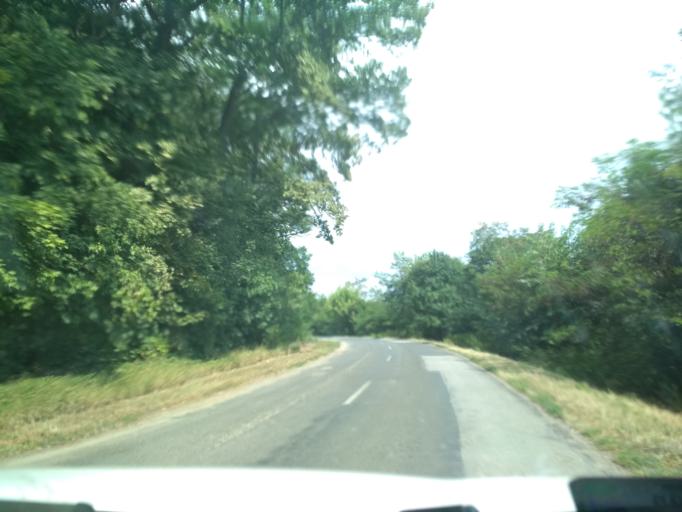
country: HU
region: Jasz-Nagykun-Szolnok
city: Tiszaszolos
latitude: 47.5204
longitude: 20.6633
